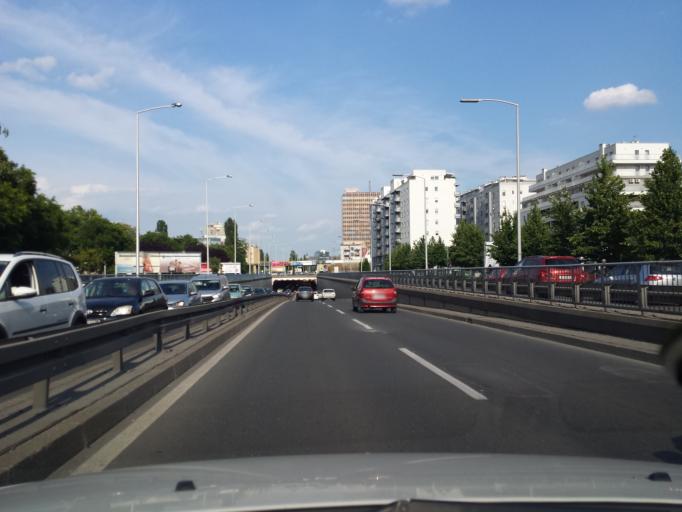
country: HR
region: Grad Zagreb
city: Zagreb - Centar
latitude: 45.7943
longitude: 15.9532
